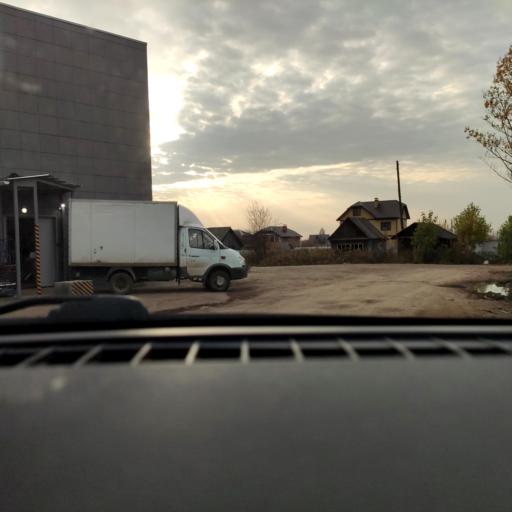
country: RU
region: Perm
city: Froly
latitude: 57.9238
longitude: 56.2721
